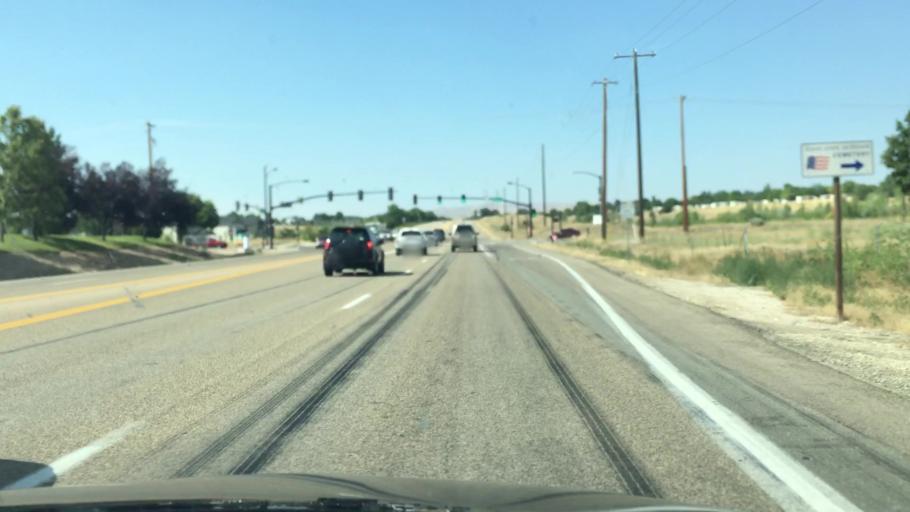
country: US
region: Idaho
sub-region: Ada County
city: Eagle
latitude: 43.6925
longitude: -116.3191
